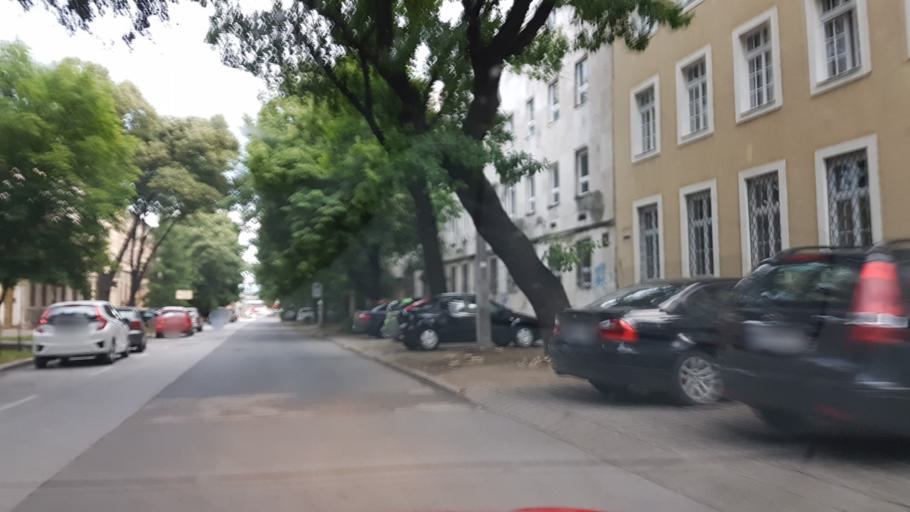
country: HU
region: Borsod-Abauj-Zemplen
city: Miskolc
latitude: 48.1053
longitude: 20.7859
